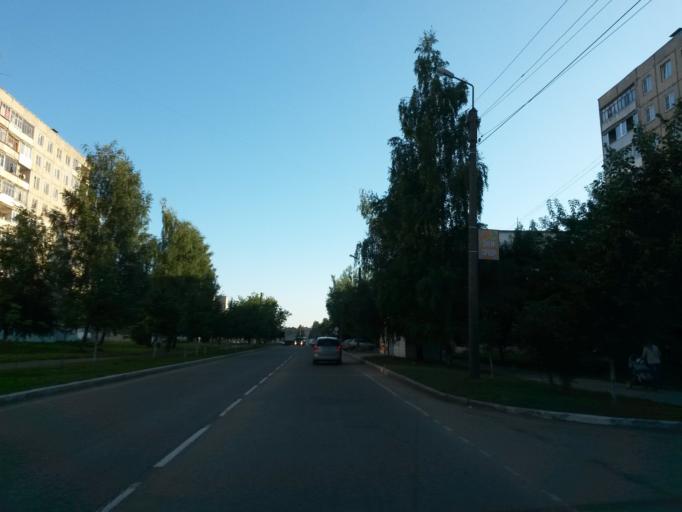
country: RU
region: Jaroslavl
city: Tutayev
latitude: 57.8682
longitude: 39.5180
